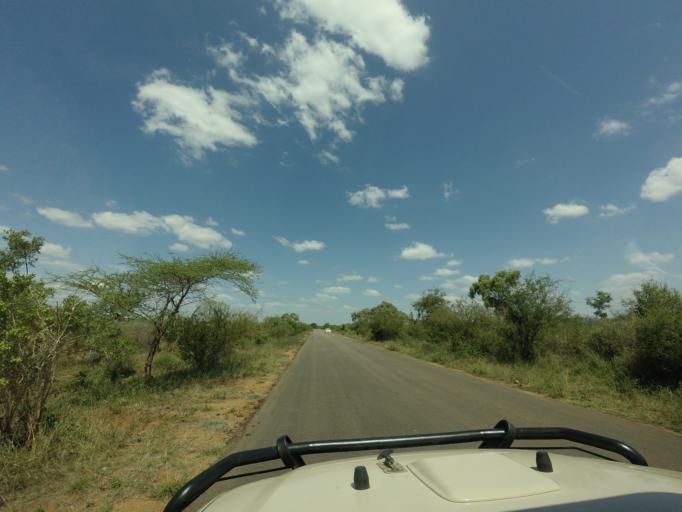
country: ZA
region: Mpumalanga
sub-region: Ehlanzeni District
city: Komatipoort
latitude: -25.1043
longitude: 31.8990
